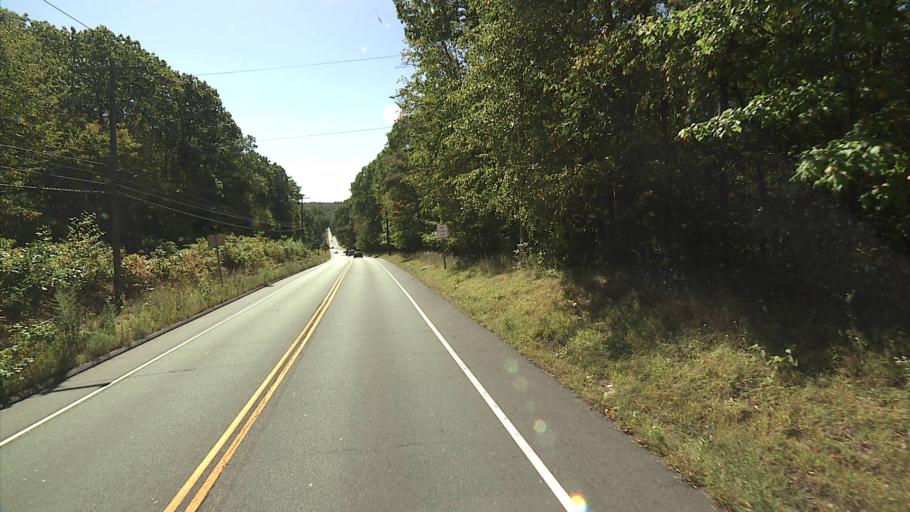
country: US
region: Connecticut
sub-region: New Haven County
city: Prospect
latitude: 41.4920
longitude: -72.9749
